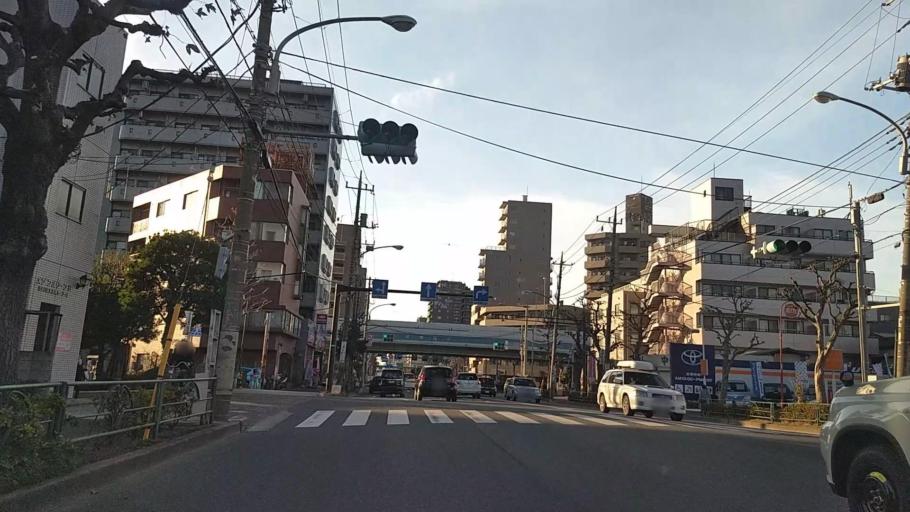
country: JP
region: Tokyo
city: Urayasu
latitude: 35.6674
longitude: 139.8745
